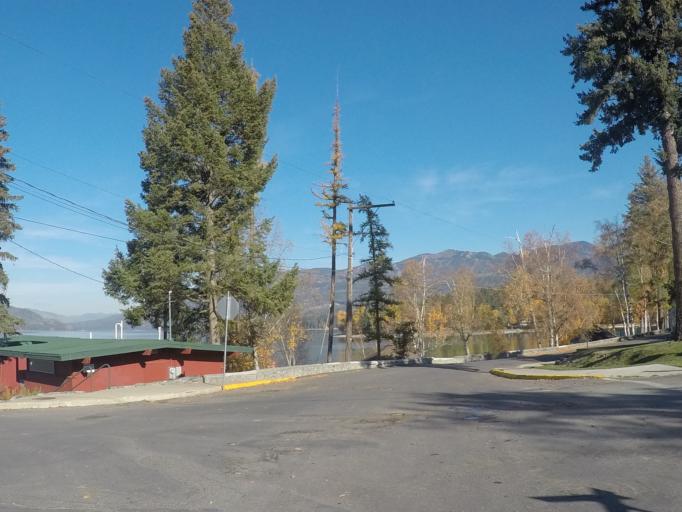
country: US
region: Montana
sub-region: Flathead County
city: Whitefish
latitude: 48.4169
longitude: -114.3507
